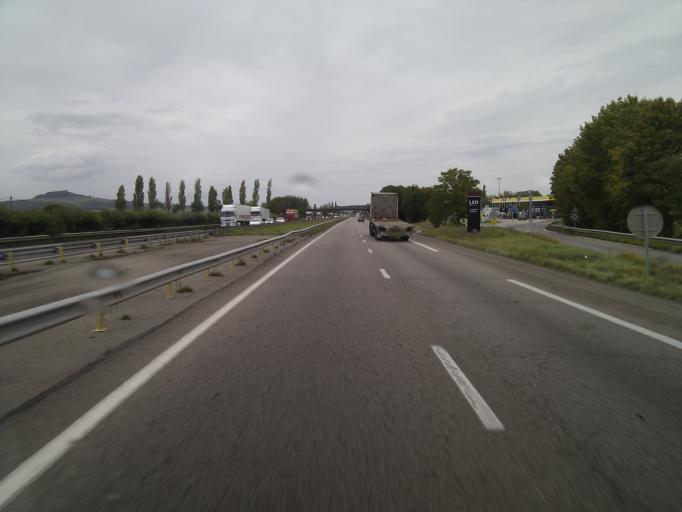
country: FR
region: Lorraine
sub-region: Departement de Meurthe-et-Moselle
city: Dieulouard
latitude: 48.8591
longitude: 6.0905
